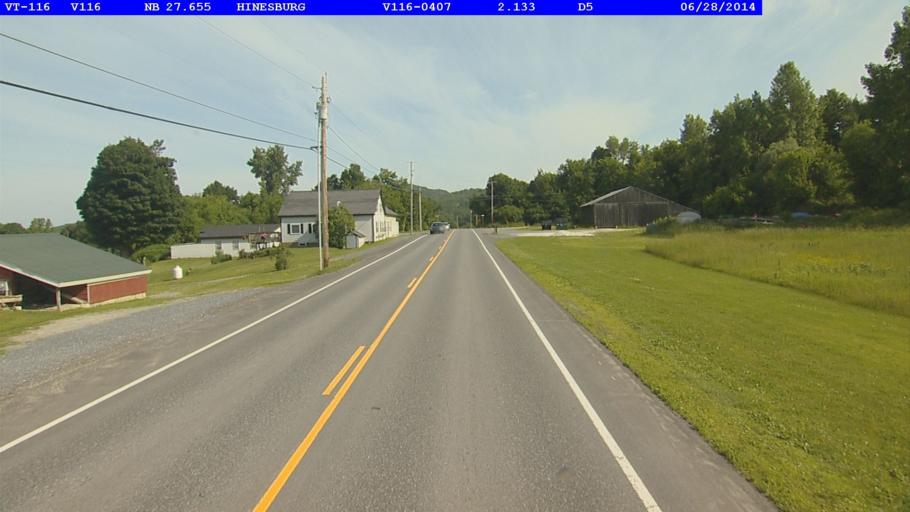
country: US
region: Vermont
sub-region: Chittenden County
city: Hinesburg
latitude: 44.3102
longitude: -73.0755
